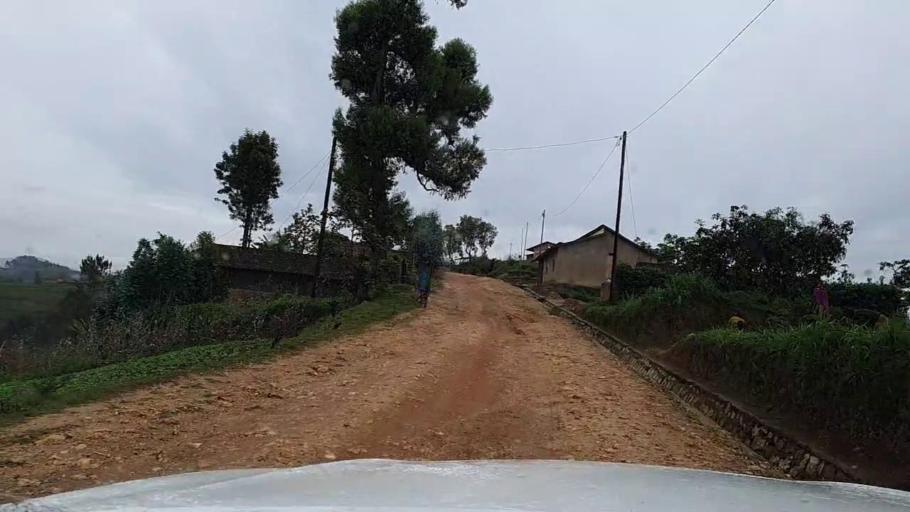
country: RW
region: Southern Province
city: Nzega
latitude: -2.4677
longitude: 29.4974
